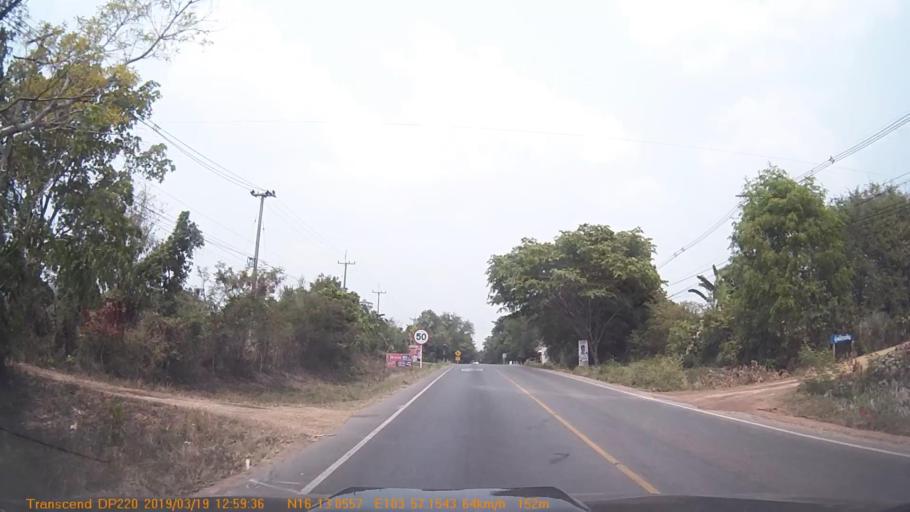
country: TH
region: Roi Et
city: Waeng
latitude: 16.2179
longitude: 103.9526
